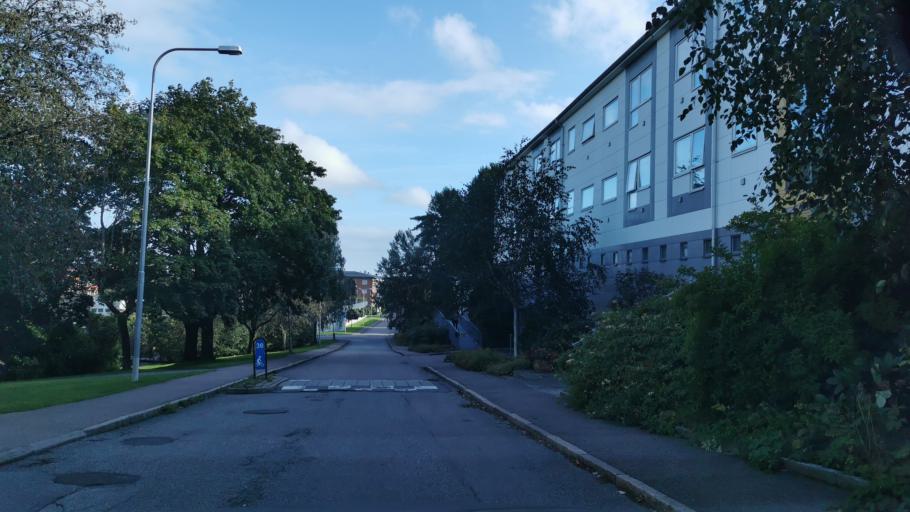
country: SE
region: Vaestra Goetaland
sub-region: Goteborg
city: Majorna
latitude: 57.6663
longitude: 11.9188
